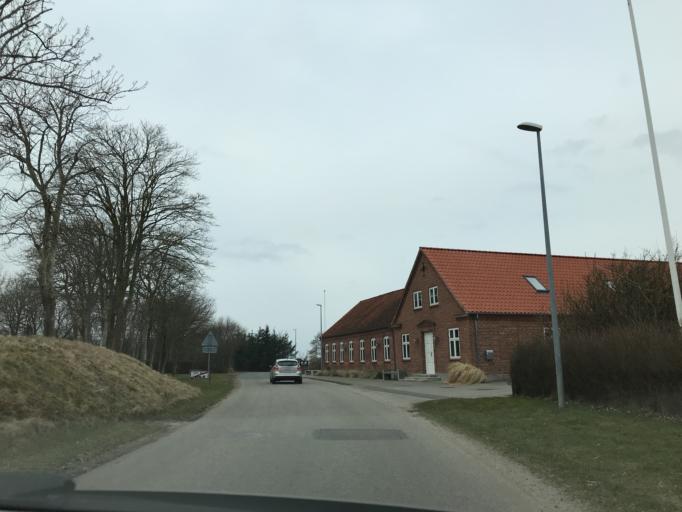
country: DK
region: South Denmark
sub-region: Varde Kommune
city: Oksbol
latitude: 55.8122
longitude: 8.2948
